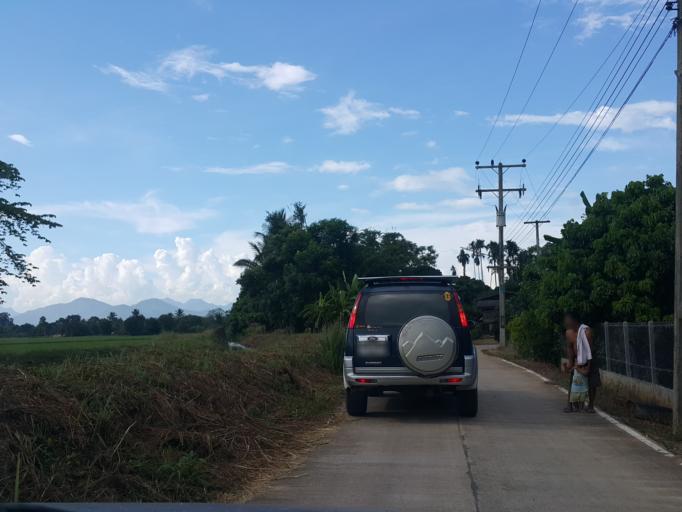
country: TH
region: Chiang Mai
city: Phrao
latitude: 19.3399
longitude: 99.1844
